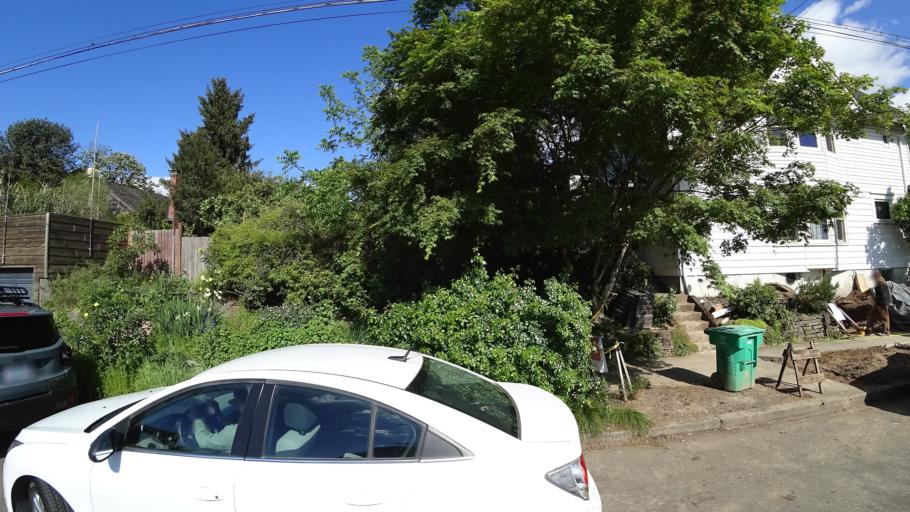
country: US
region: Oregon
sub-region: Multnomah County
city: Portland
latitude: 45.5182
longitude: -122.6516
